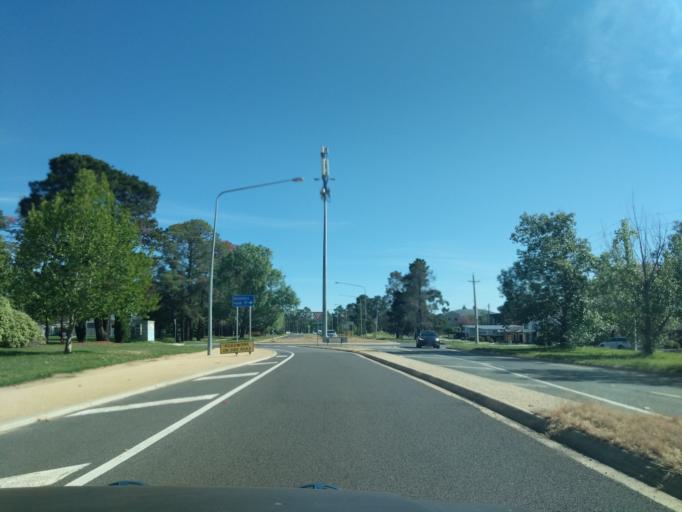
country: AU
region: Australian Capital Territory
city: Forrest
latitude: -35.3381
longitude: 149.1499
